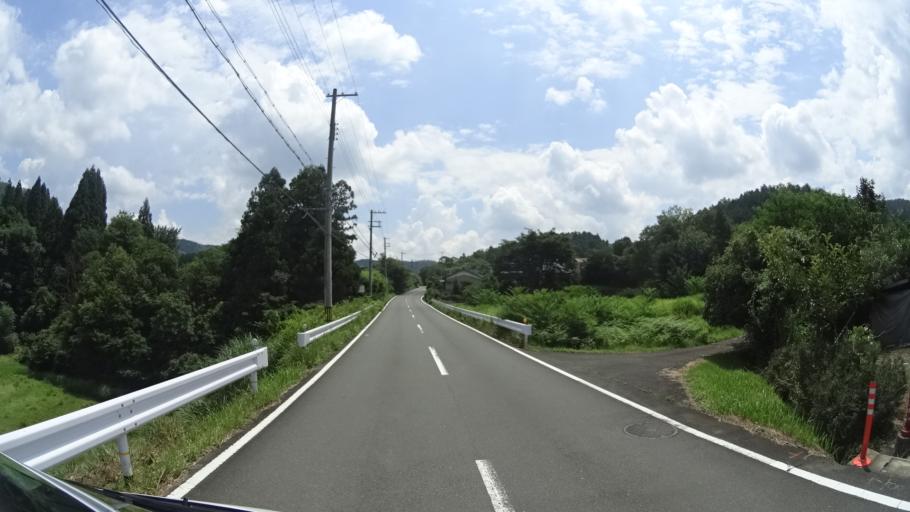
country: JP
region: Kyoto
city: Ayabe
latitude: 35.1859
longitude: 135.2723
